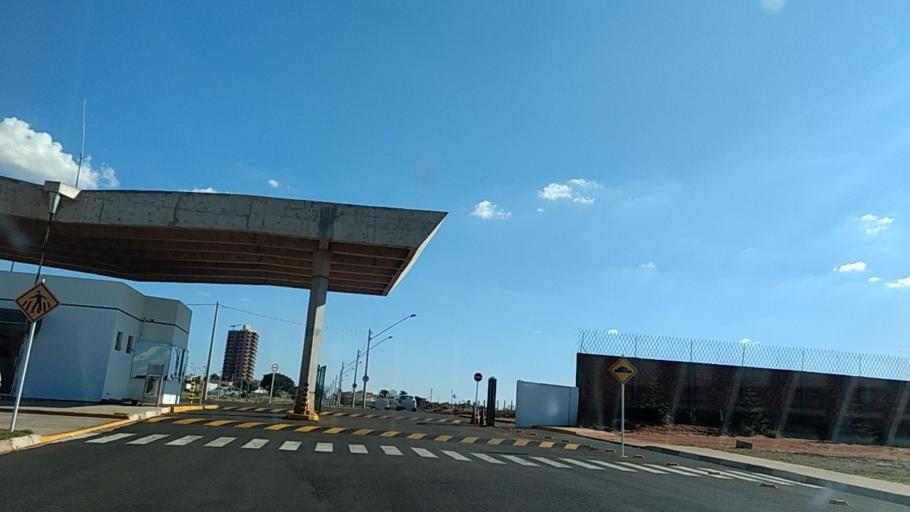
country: BR
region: Sao Paulo
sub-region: Botucatu
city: Botucatu
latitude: -22.8505
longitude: -48.4356
